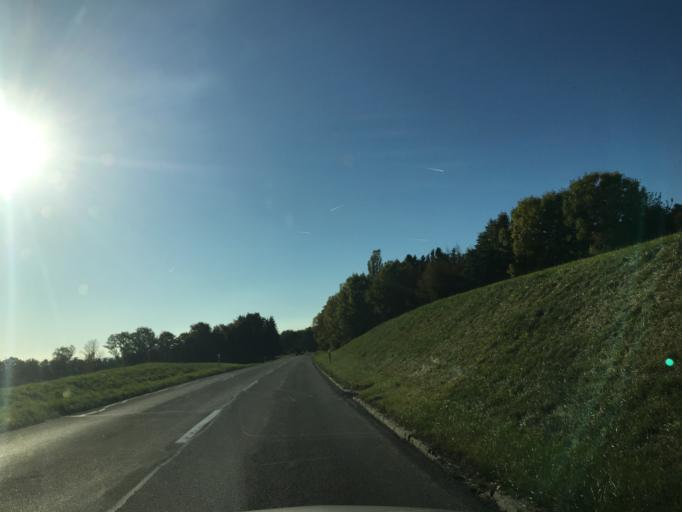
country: CH
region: Vaud
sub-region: Lavaux-Oron District
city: Oron-la-ville
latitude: 46.5834
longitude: 6.8848
